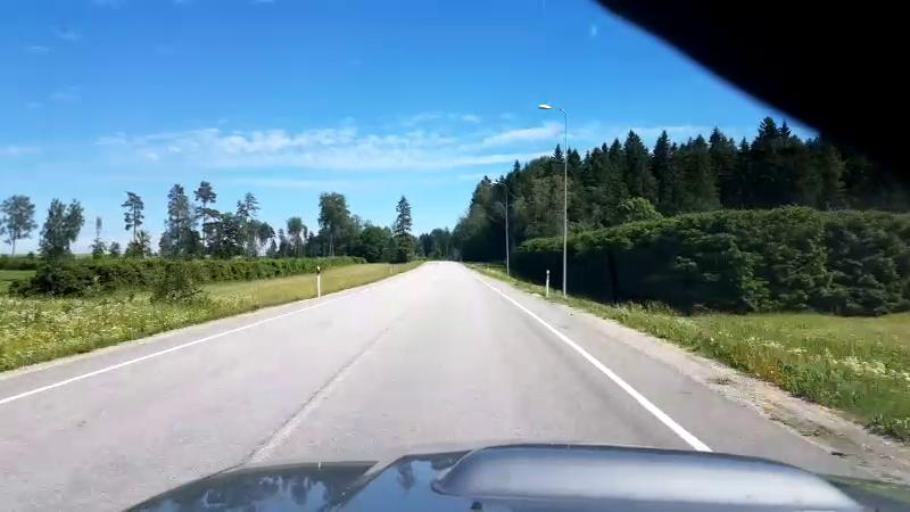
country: EE
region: Jaervamaa
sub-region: Koeru vald
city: Koeru
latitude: 58.9818
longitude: 26.0483
